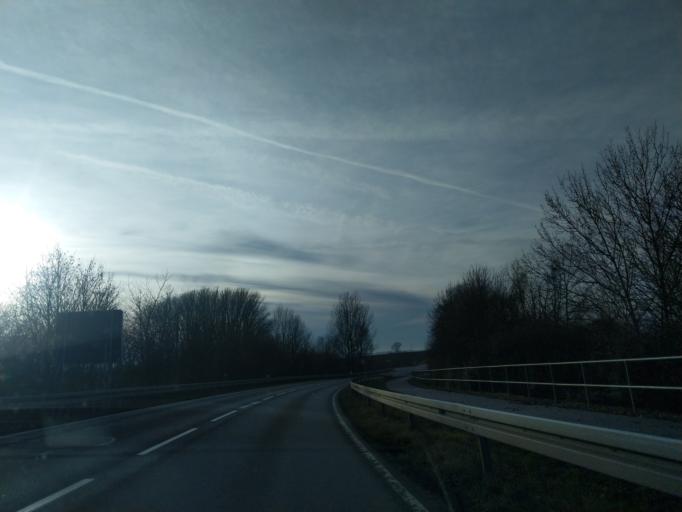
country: DE
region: Bavaria
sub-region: Lower Bavaria
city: Osterhofen
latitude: 48.7009
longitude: 13.0027
